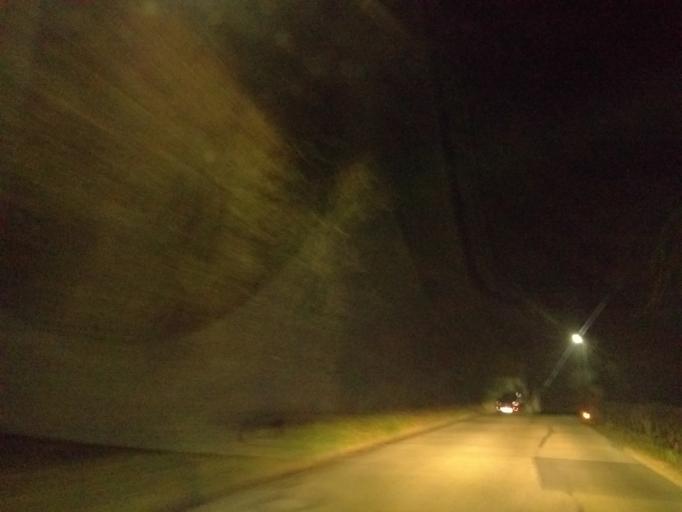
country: DE
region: Bavaria
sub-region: Swabia
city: Donauwoerth
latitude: 48.7101
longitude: 10.7488
